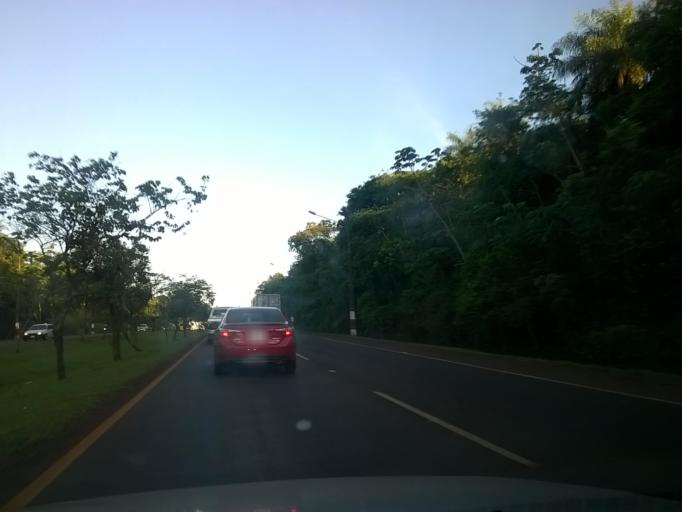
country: PY
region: Alto Parana
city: Ciudad del Este
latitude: -25.4476
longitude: -54.6296
